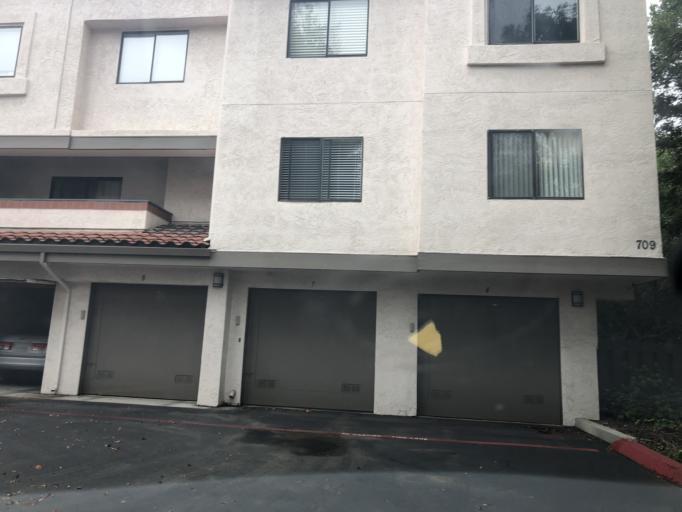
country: US
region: California
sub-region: Santa Clara County
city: Sunnyvale
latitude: 37.3927
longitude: -122.0154
